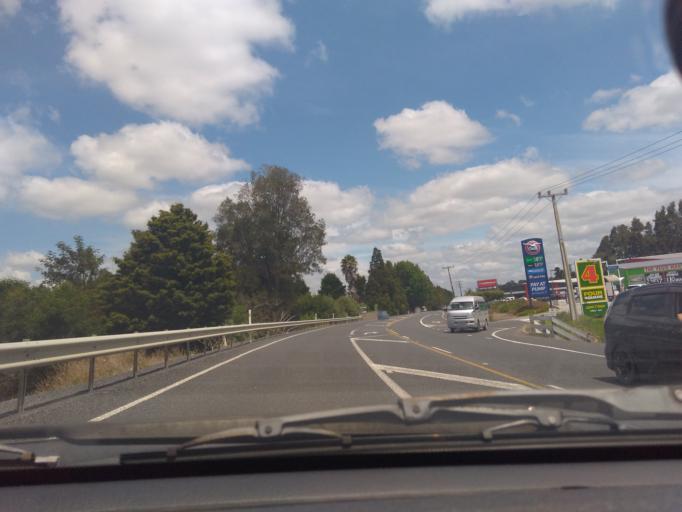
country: NZ
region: Northland
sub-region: Far North District
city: Kerikeri
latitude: -35.2091
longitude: 173.9201
